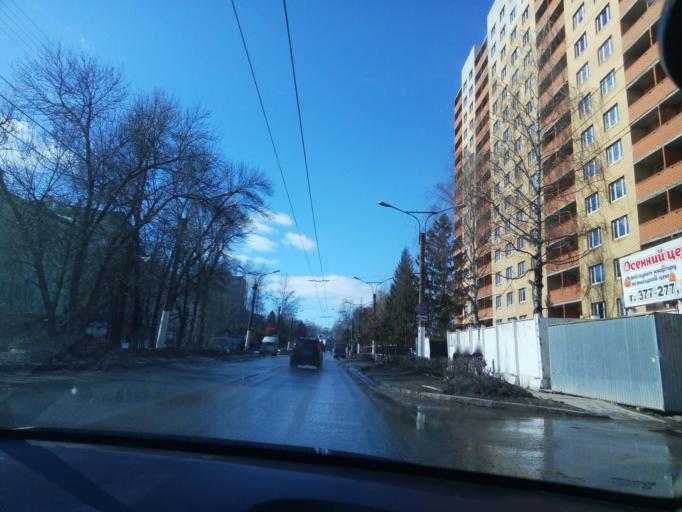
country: RU
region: Chuvashia
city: Novyye Lapsary
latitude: 56.1086
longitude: 47.1774
